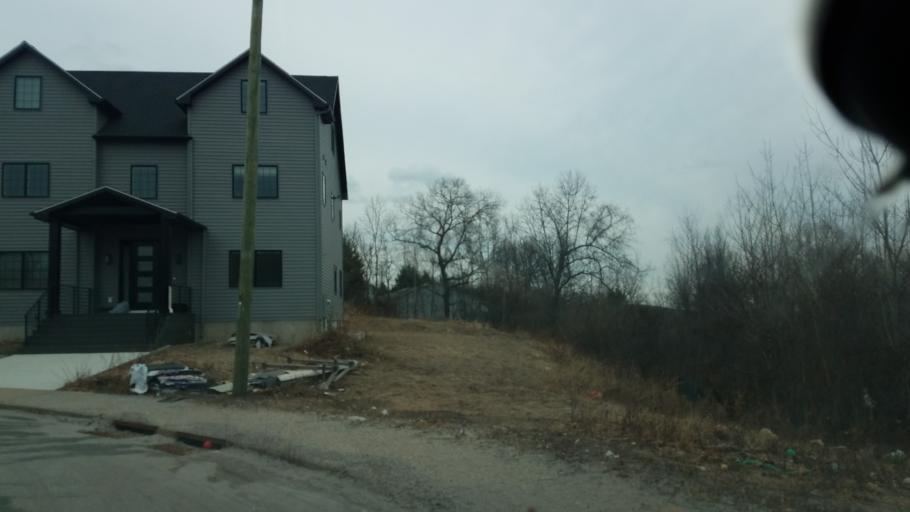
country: US
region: Connecticut
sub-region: New Haven County
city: Waterbury
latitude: 41.5912
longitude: -73.0325
